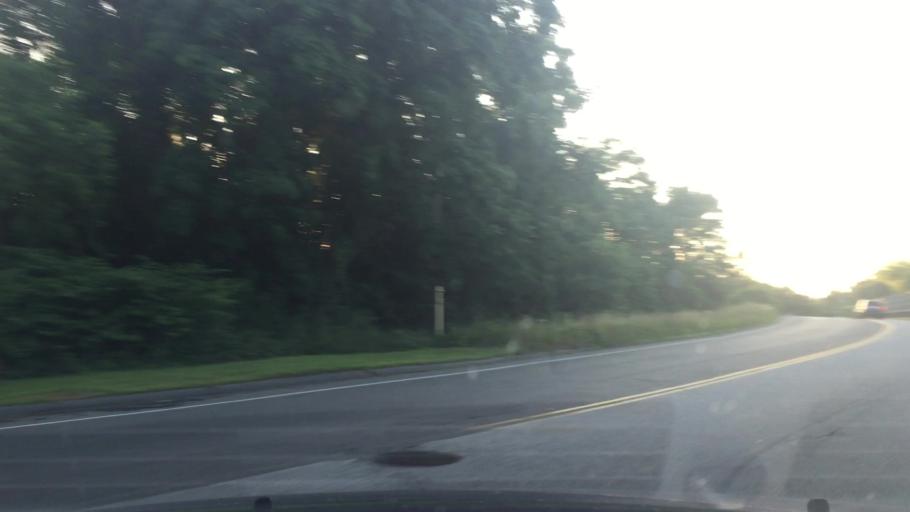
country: US
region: Massachusetts
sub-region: Essex County
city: Haverhill
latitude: 42.8033
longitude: -71.0833
